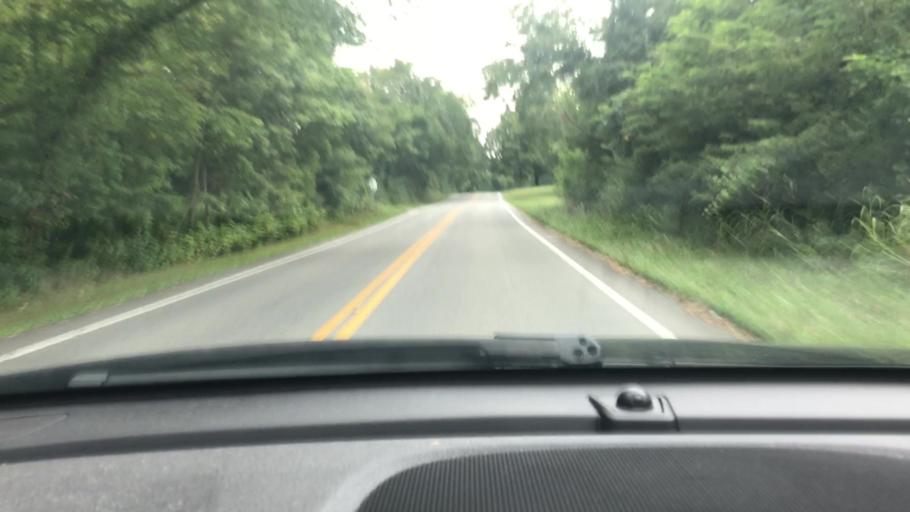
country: US
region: Tennessee
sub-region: Cheatham County
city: Ashland City
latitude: 36.2727
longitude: -87.1936
